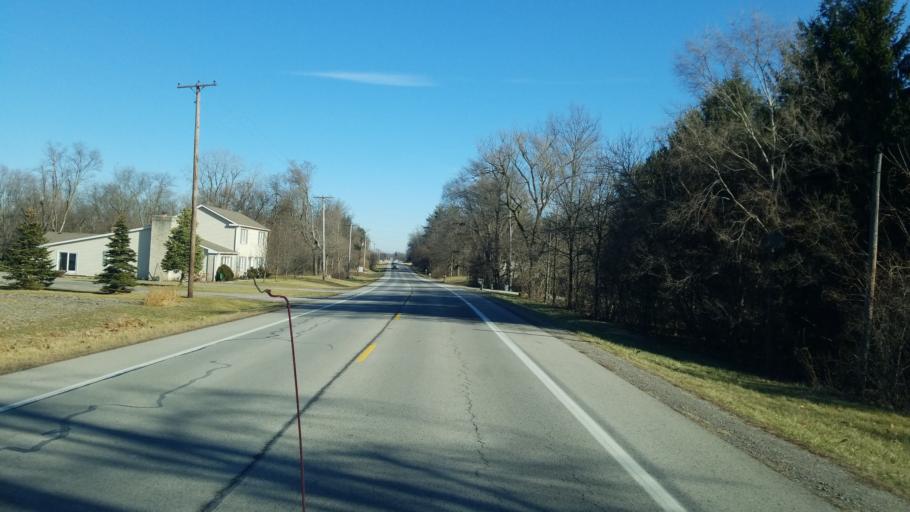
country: US
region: Ohio
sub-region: Lucas County
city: Whitehouse
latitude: 41.4315
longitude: -83.8358
